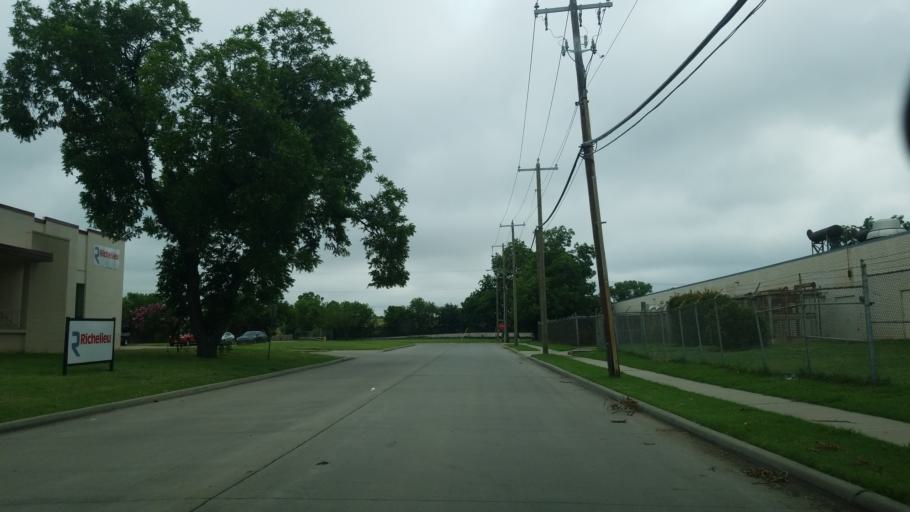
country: US
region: Texas
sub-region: Dallas County
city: Irving
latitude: 32.8364
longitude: -96.8801
